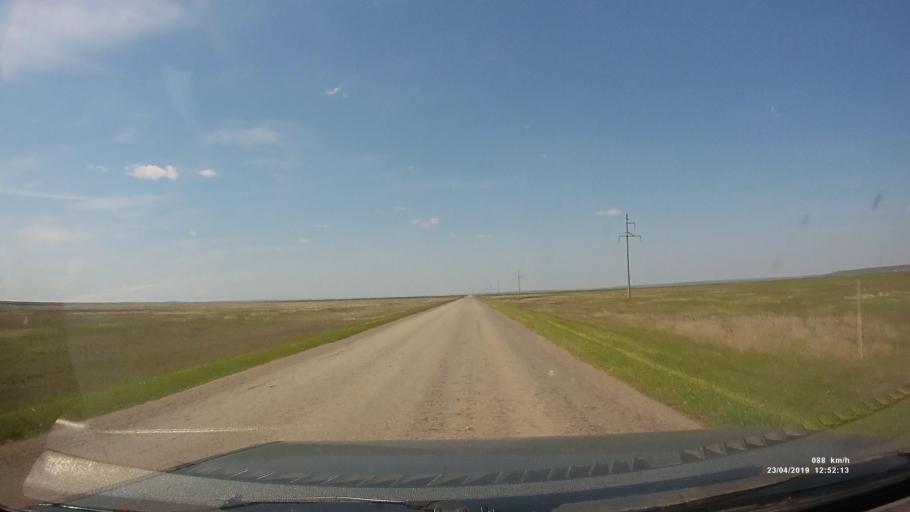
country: RU
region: Kalmykiya
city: Yashalta
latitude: 46.5625
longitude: 42.6125
